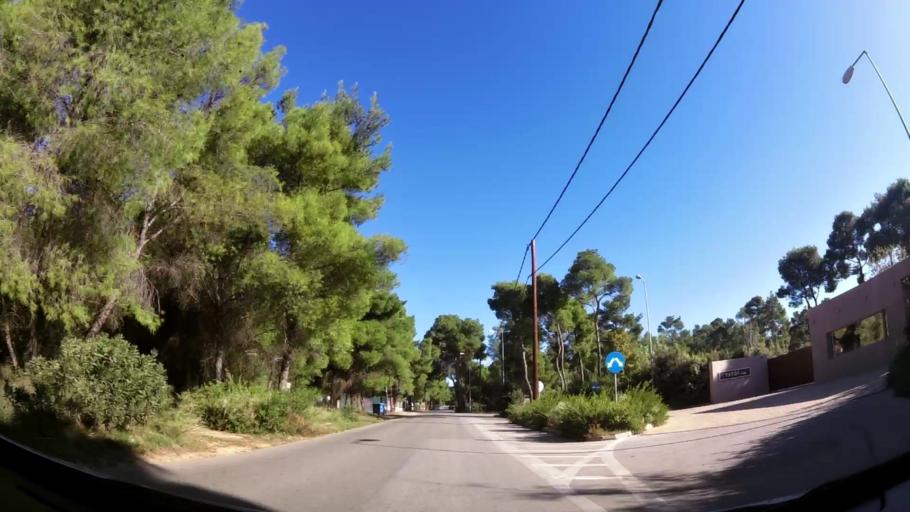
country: GR
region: Attica
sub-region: Nomarchia Anatolikis Attikis
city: Varybobi
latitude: 38.1213
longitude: 23.7916
